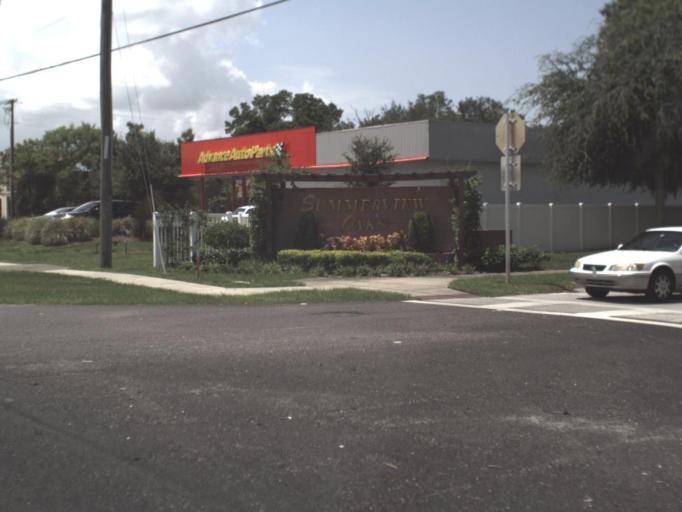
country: US
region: Florida
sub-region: Hillsborough County
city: Riverview
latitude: 27.7965
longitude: -82.3350
